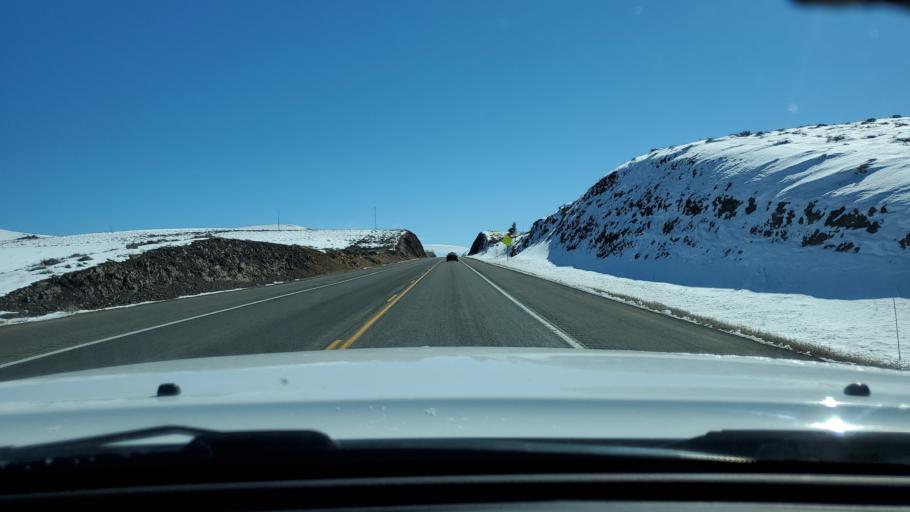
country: US
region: Colorado
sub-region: Gunnison County
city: Gunnison
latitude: 38.5180
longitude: -106.7673
